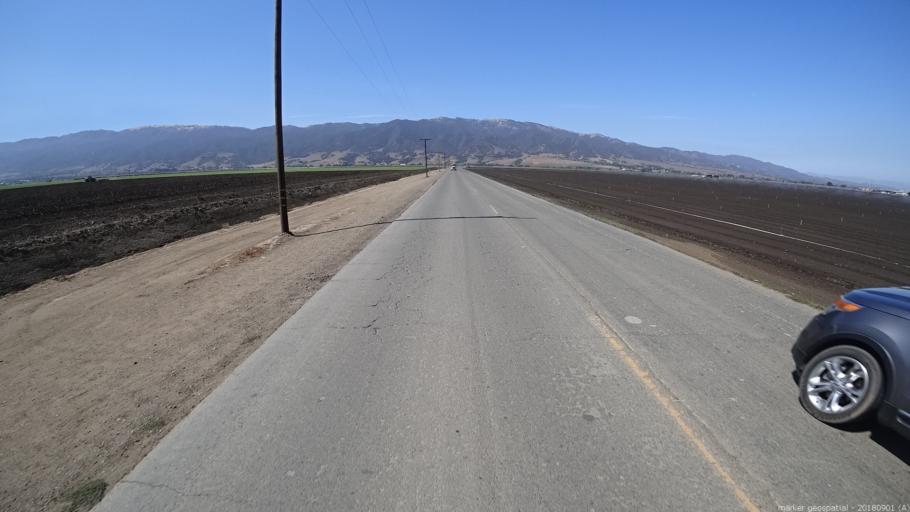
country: US
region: California
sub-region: Monterey County
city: Chualar
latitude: 36.5615
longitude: -121.5236
